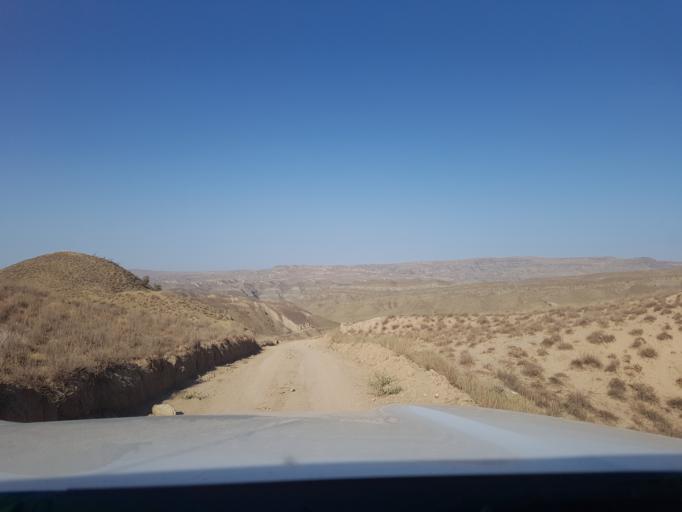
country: TM
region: Balkan
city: Magtymguly
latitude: 38.3007
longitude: 56.7895
